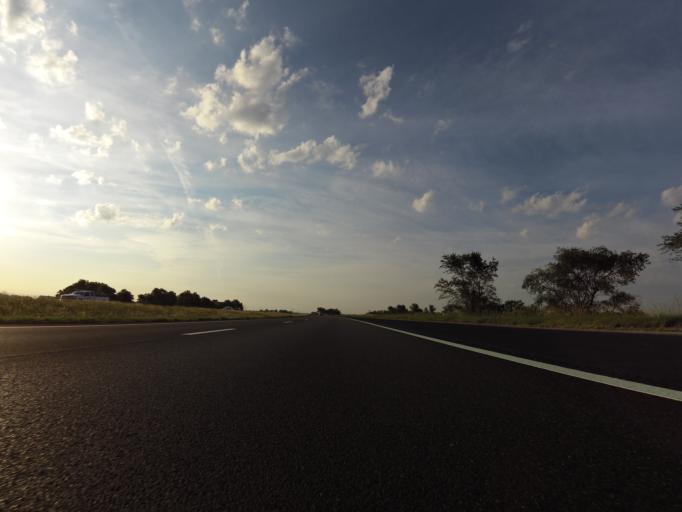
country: US
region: Kansas
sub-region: Sedgwick County
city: Maize
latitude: 37.8036
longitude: -97.4951
